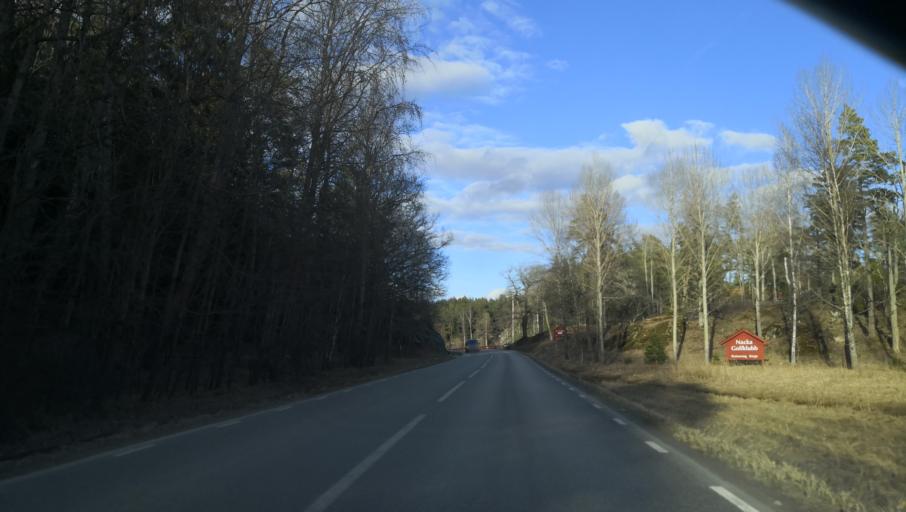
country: SE
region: Stockholm
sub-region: Varmdo Kommun
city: Gustavsberg
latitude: 59.3373
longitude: 18.3514
